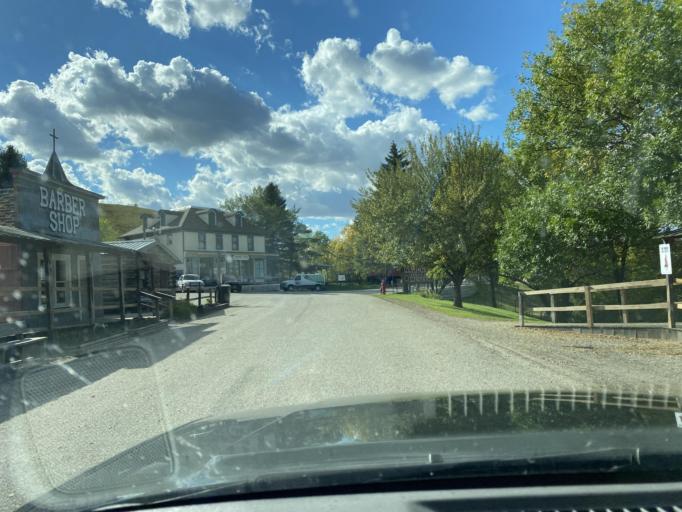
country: US
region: North Dakota
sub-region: Stutsman County
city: Jamestown
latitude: 46.8896
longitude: -98.7006
